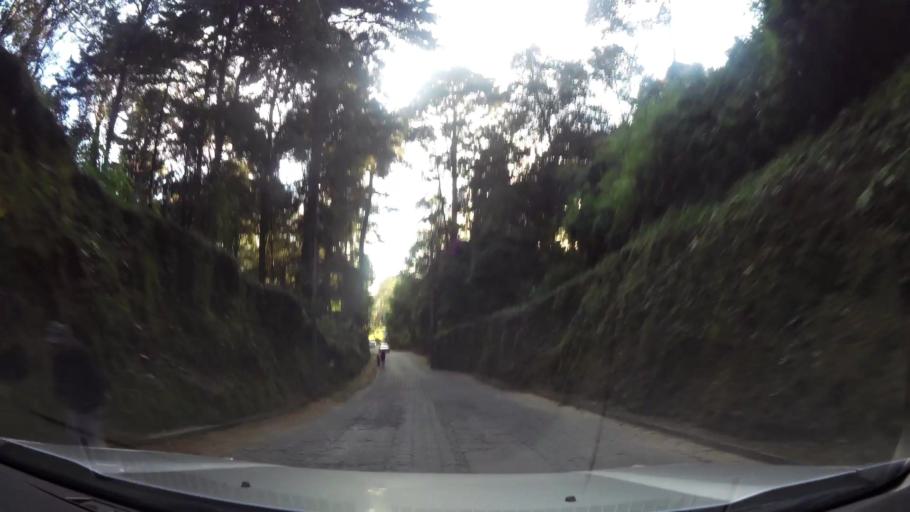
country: GT
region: Sacatepequez
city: San Lucas Sacatepequez
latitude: 14.6157
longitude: -90.6502
